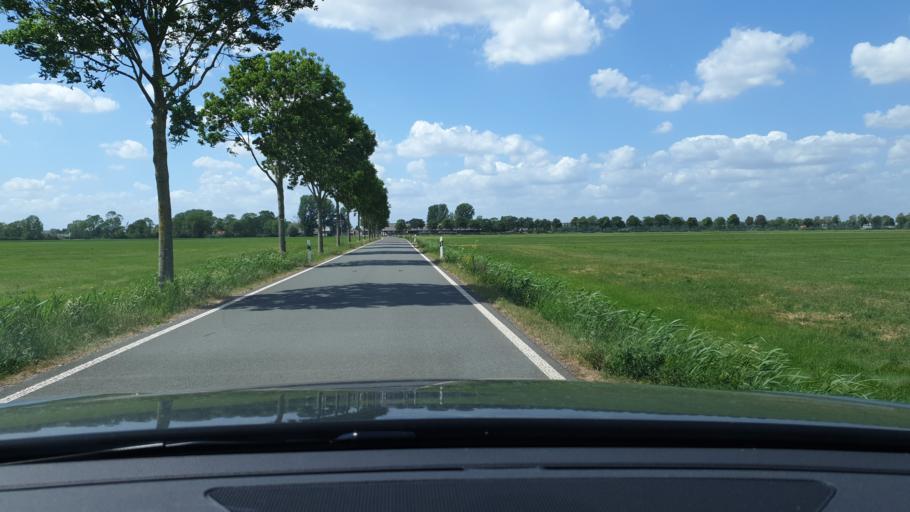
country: DE
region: North Rhine-Westphalia
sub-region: Regierungsbezirk Dusseldorf
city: Kranenburg
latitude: 51.8257
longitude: 6.0386
